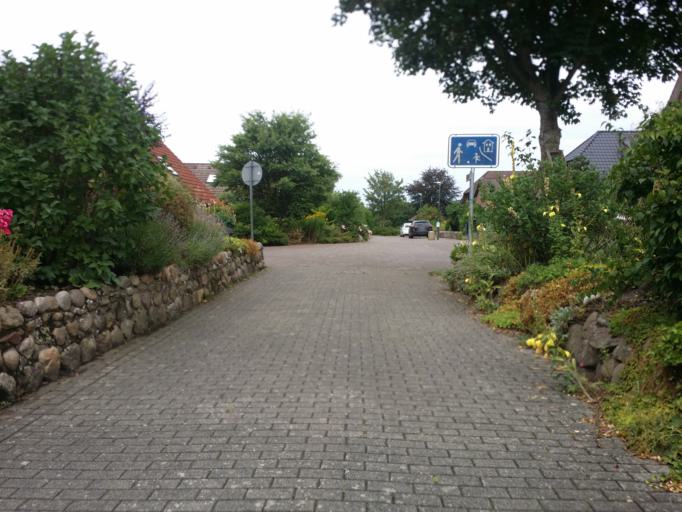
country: DE
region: Schleswig-Holstein
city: Oldendorf
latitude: 53.9488
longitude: 9.4590
